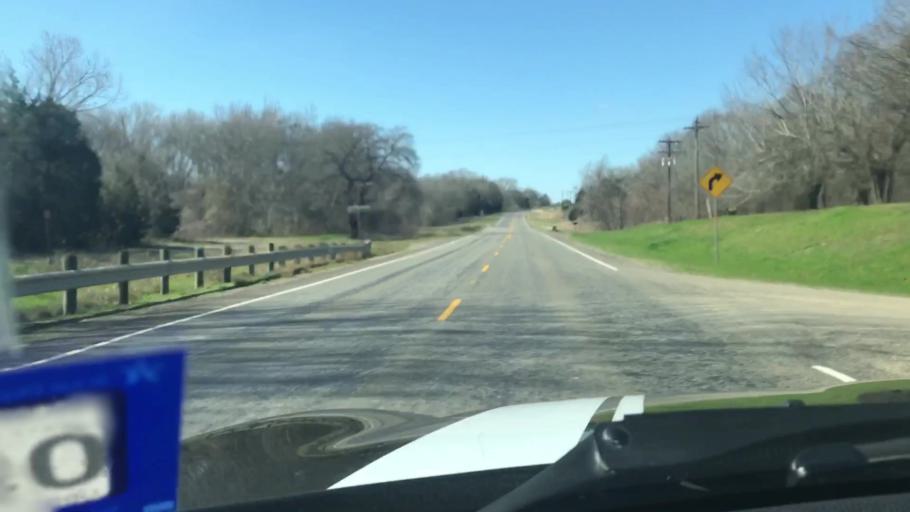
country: US
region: Texas
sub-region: Robertson County
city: Calvert
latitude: 30.8848
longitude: -96.7621
